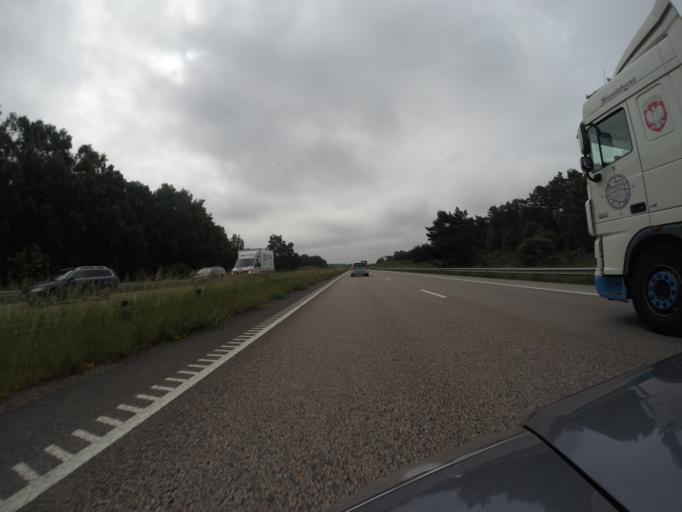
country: SE
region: Skane
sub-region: Kavlinge Kommun
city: Hofterup
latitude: 55.8056
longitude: 12.9542
